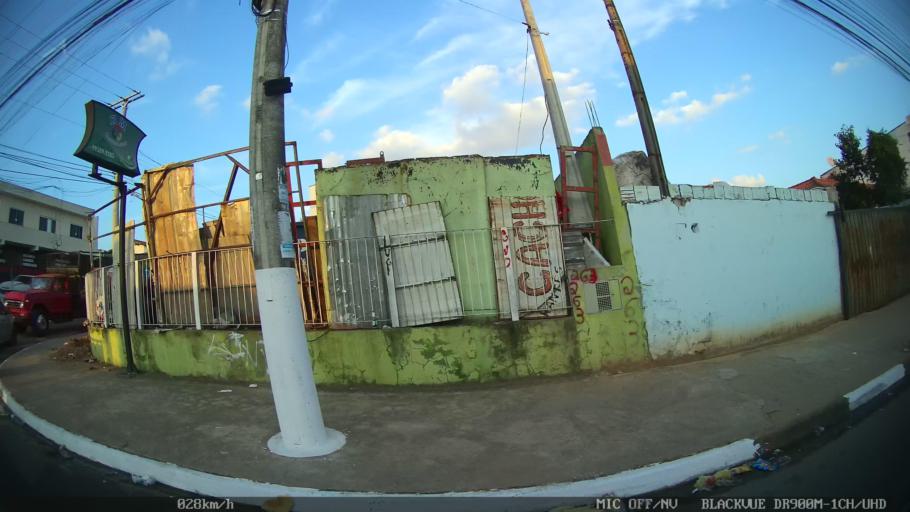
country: BR
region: Sao Paulo
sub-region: Hortolandia
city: Hortolandia
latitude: -22.8515
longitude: -47.2053
